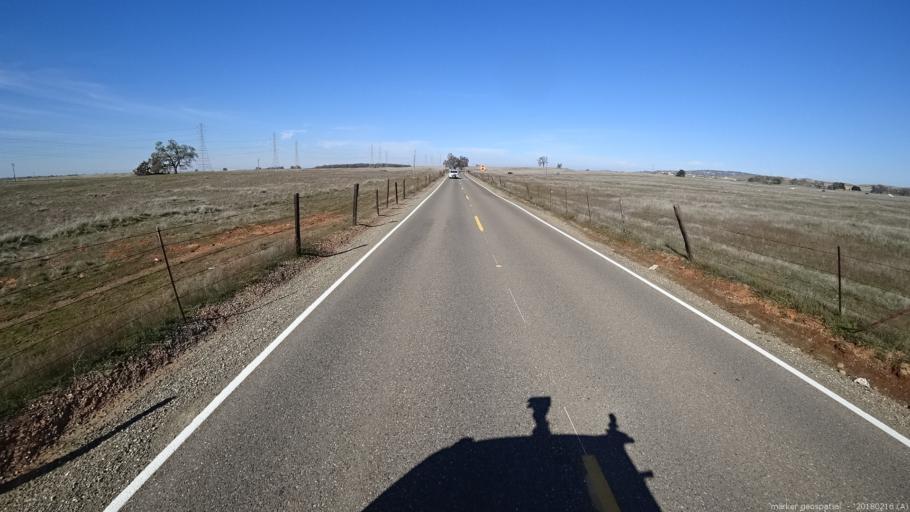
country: US
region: California
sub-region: Sacramento County
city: Folsom
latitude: 38.6149
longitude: -121.1416
